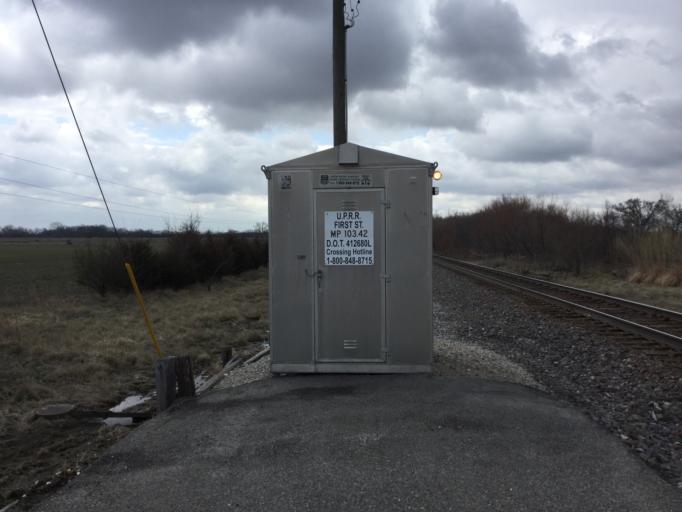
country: US
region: Kansas
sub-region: Neosho County
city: Erie
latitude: 37.7907
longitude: -95.1520
